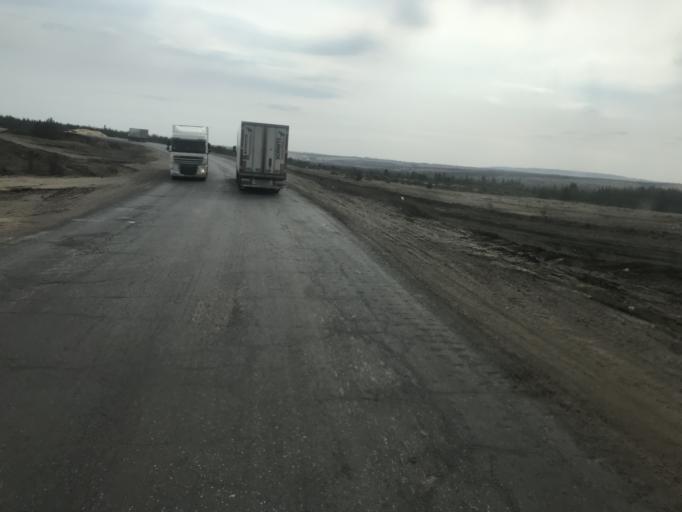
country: RU
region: Ulyanovsk
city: Novospasskoye
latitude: 53.1503
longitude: 47.6504
